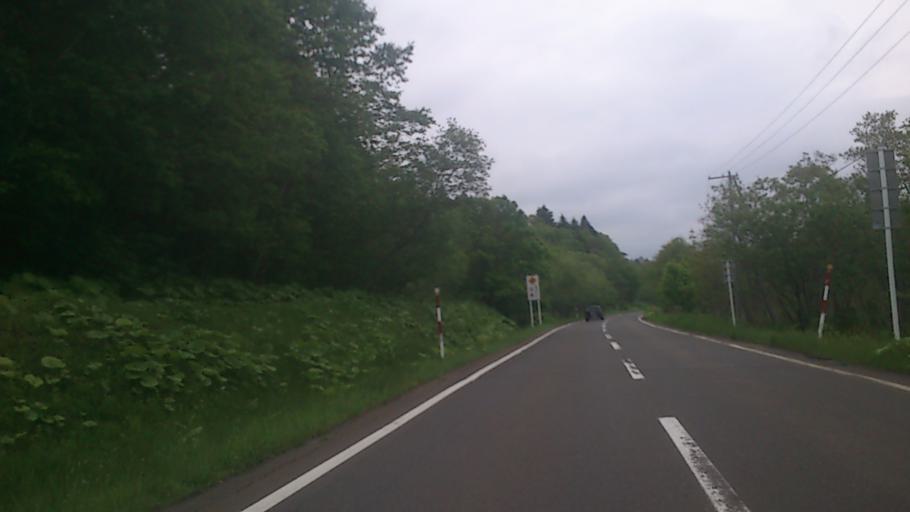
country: JP
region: Hokkaido
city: Nemuro
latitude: 43.0873
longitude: 145.0608
